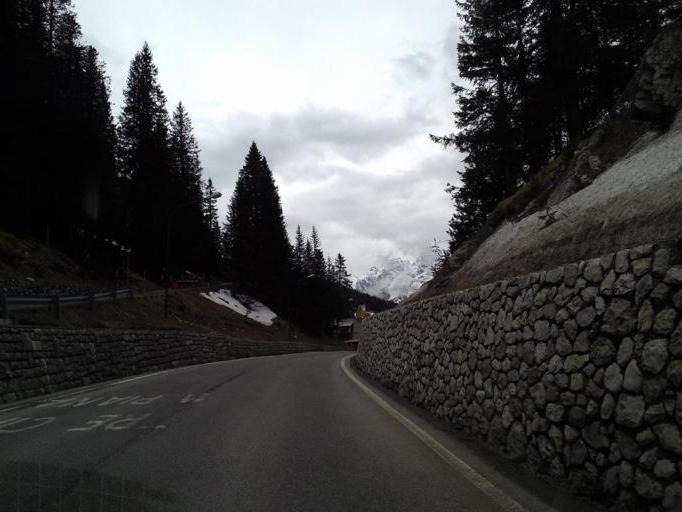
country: IT
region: Veneto
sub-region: Provincia di Belluno
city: Cortina d'Ampezzo
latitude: 46.5860
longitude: 12.2537
